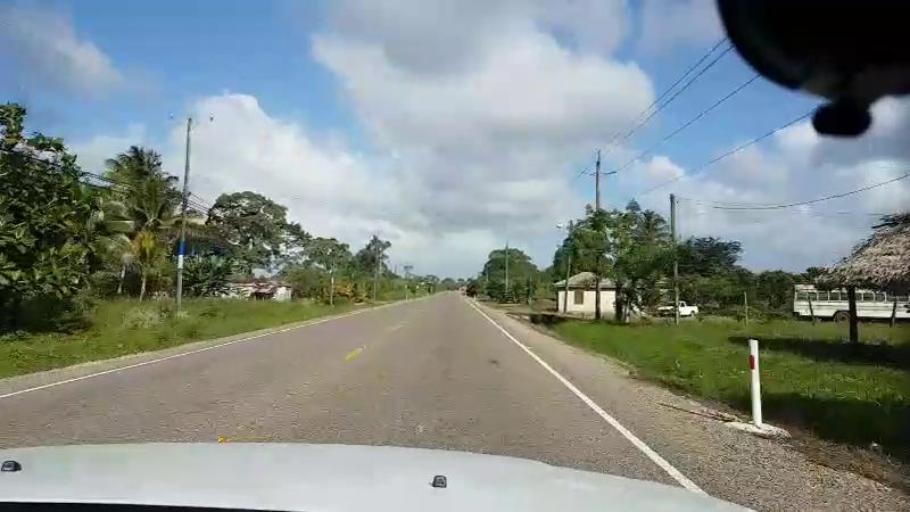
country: BZ
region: Stann Creek
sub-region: Dangriga
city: Dangriga
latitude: 16.9964
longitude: -88.3552
